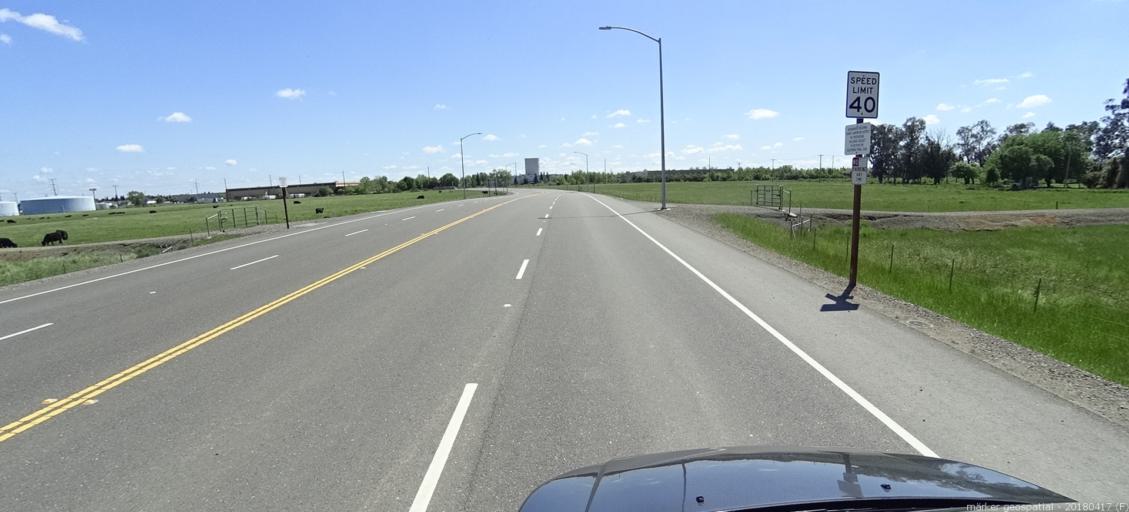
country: US
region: California
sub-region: Sacramento County
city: Laguna
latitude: 38.4340
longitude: -121.4627
